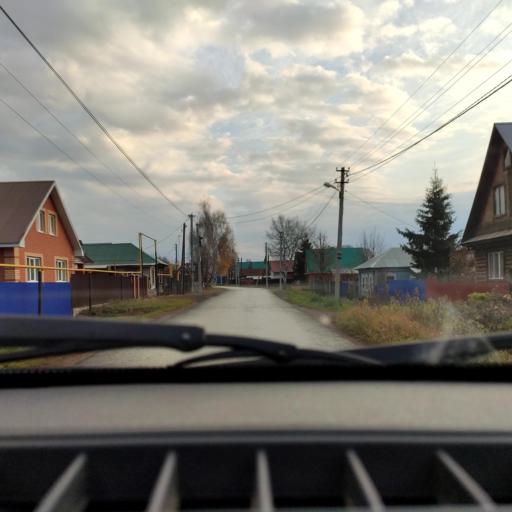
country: RU
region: Bashkortostan
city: Avdon
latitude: 54.6443
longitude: 55.7453
